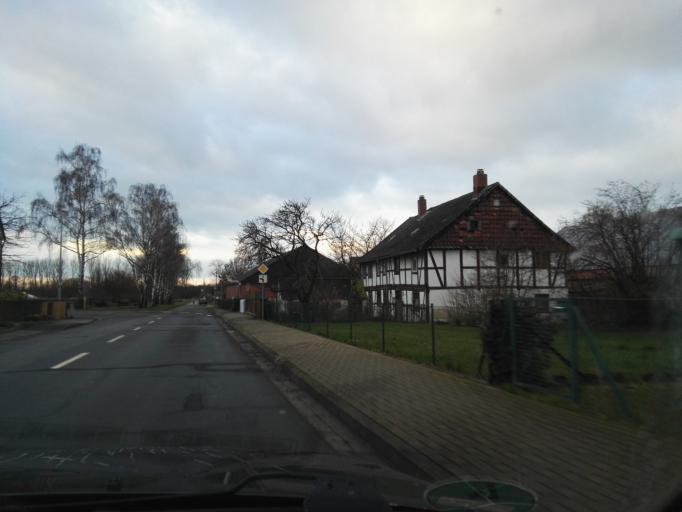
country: DE
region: Lower Saxony
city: Leiferde
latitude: 52.2252
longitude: 10.4576
